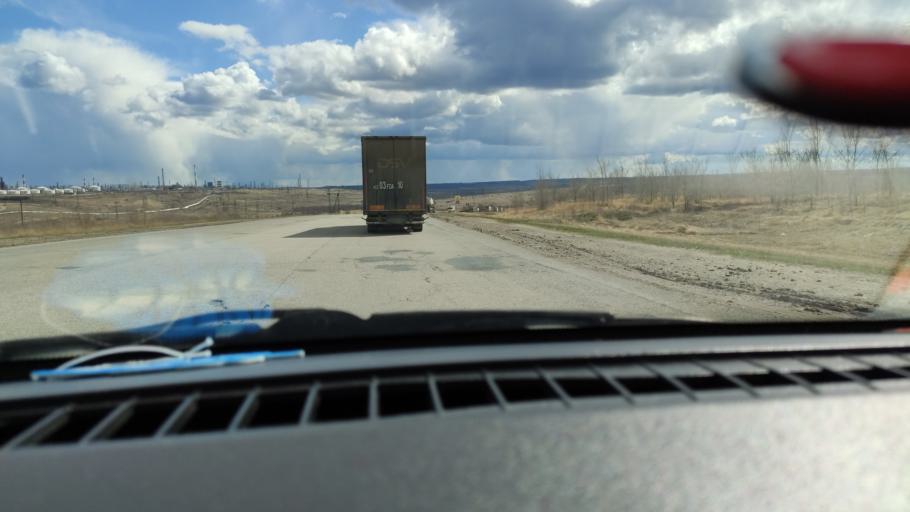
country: RU
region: Samara
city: Varlamovo
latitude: 53.1045
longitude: 48.3570
